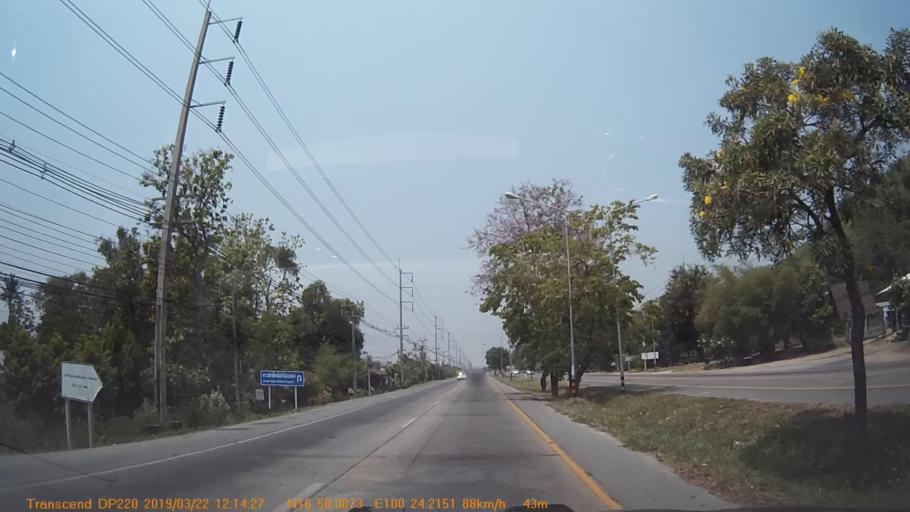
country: TH
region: Phitsanulok
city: Wang Thong
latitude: 16.8336
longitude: 100.4034
